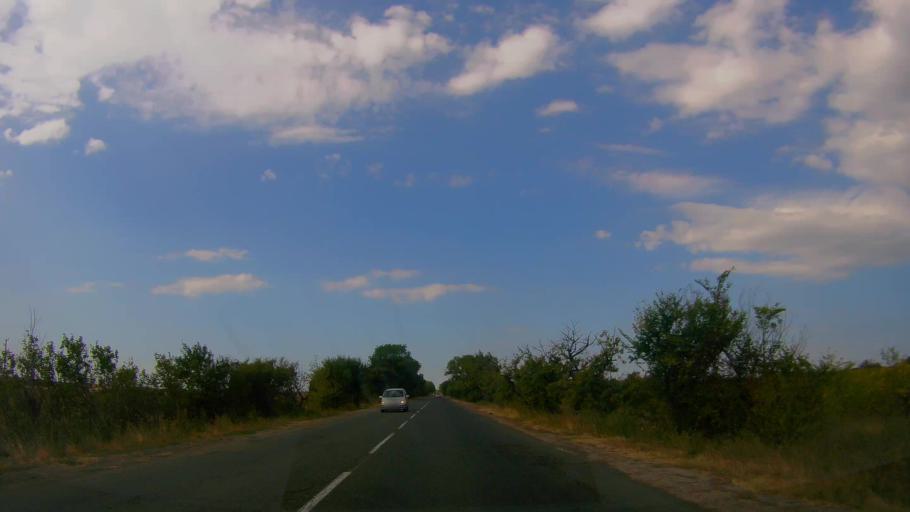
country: BG
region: Burgas
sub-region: Obshtina Aytos
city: Aytos
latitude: 42.6914
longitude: 27.1643
